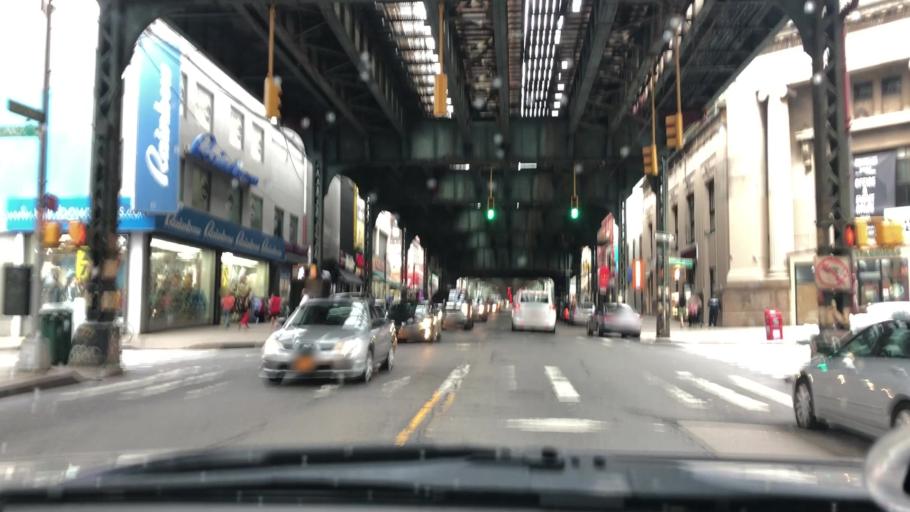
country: US
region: New York
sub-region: Queens County
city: Long Island City
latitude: 40.7004
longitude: -73.9415
